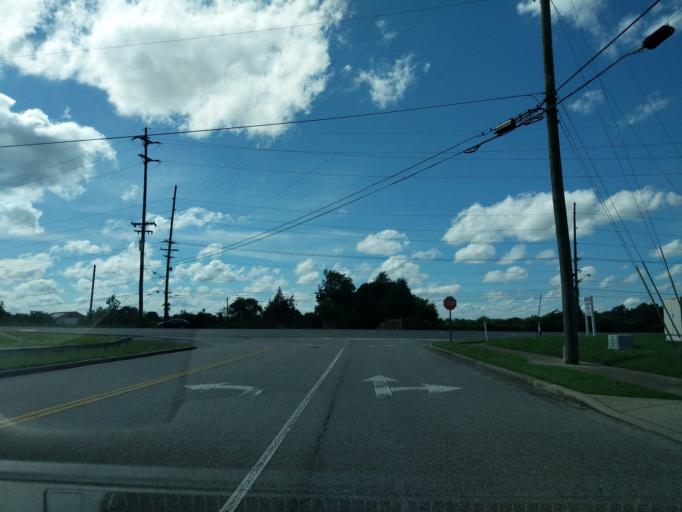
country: US
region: Tennessee
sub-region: Davidson County
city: Lakewood
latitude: 36.2663
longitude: -86.6697
